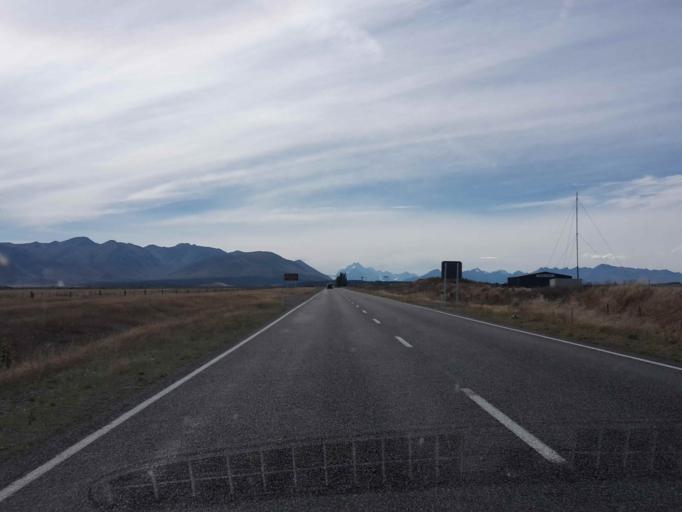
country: NZ
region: Canterbury
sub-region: Timaru District
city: Pleasant Point
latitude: -44.2459
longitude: 170.1164
